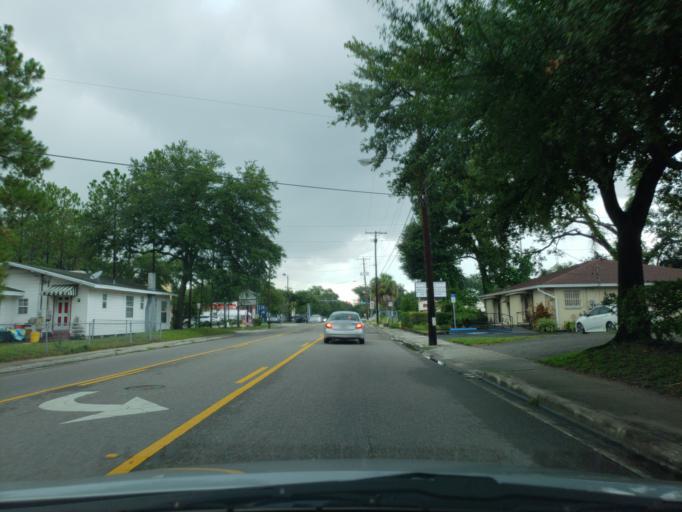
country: US
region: Florida
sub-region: Hillsborough County
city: Tampa
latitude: 27.9801
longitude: -82.4676
